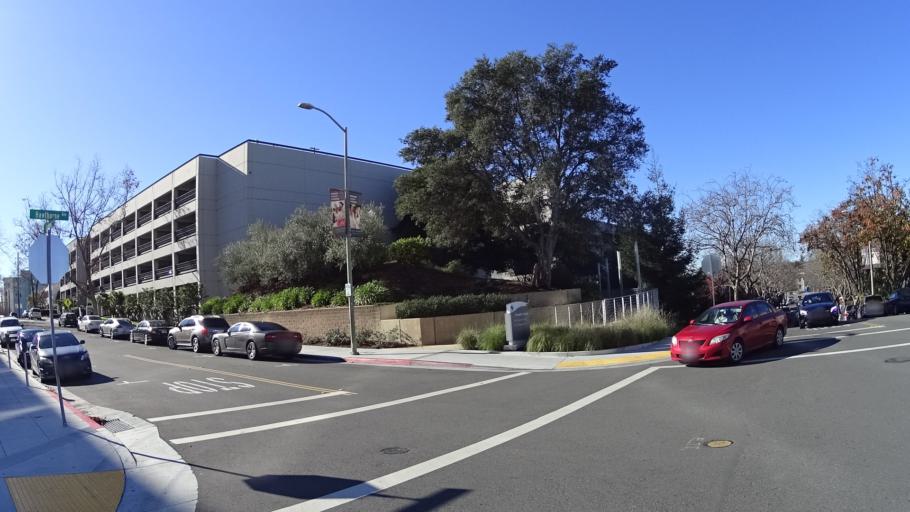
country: US
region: California
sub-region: Alameda County
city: Oakland
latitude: 37.8209
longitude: -122.2640
